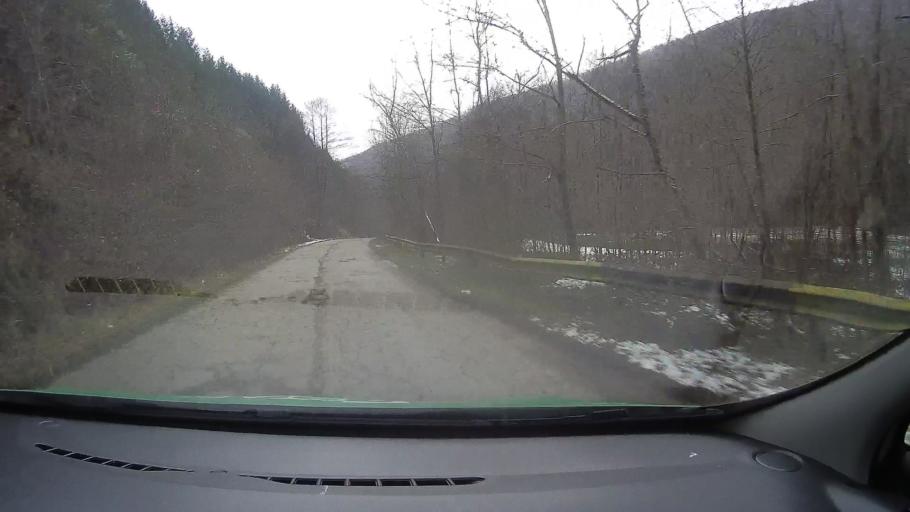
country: RO
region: Hunedoara
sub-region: Comuna Balsa
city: Balsa
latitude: 46.0029
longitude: 23.1502
